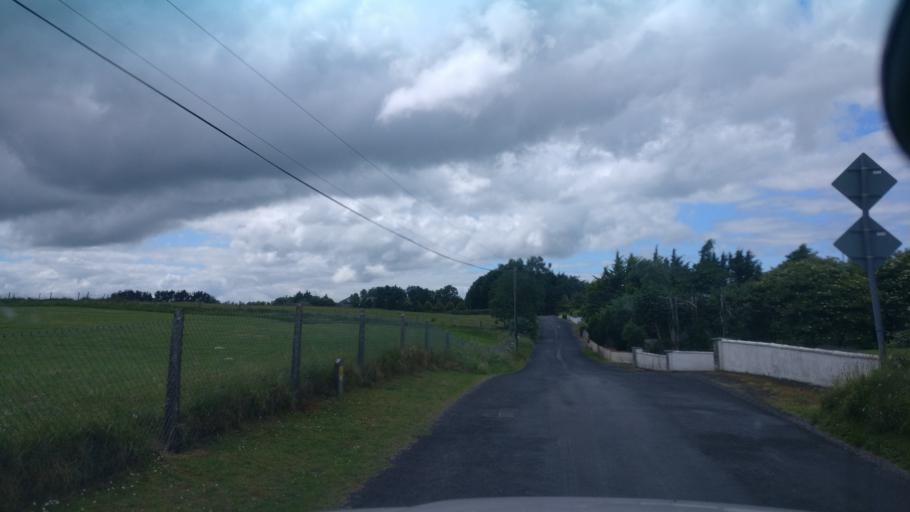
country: IE
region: Connaught
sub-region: County Galway
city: Loughrea
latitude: 53.1702
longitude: -8.5531
